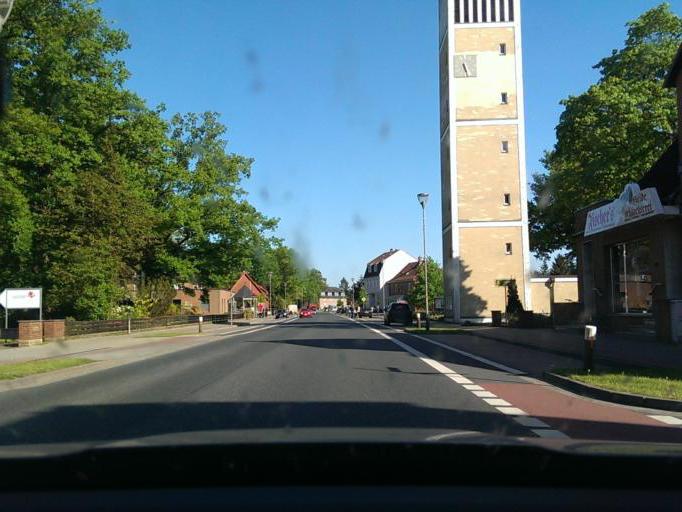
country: DE
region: Lower Saxony
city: Wietze
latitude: 52.6541
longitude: 9.8412
